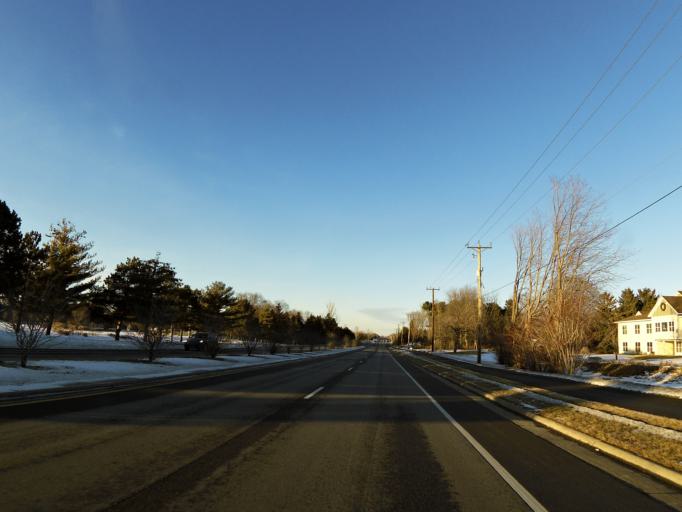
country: US
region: Minnesota
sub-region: Washington County
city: Woodbury
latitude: 44.8957
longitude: -92.9033
